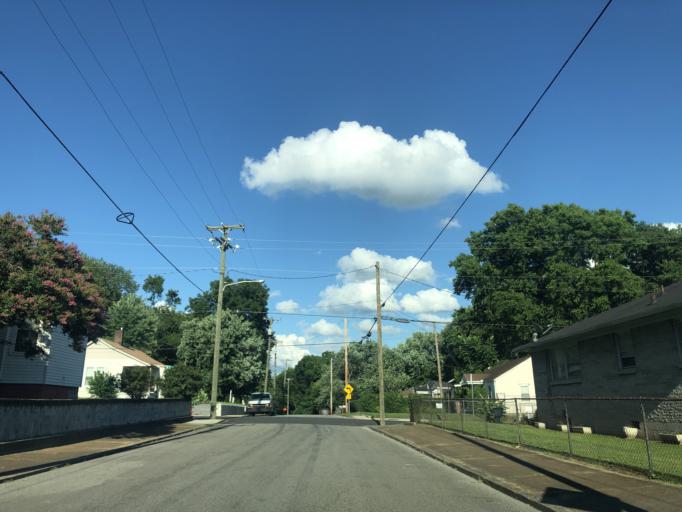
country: US
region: Tennessee
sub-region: Davidson County
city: Nashville
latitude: 36.1842
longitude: -86.7640
